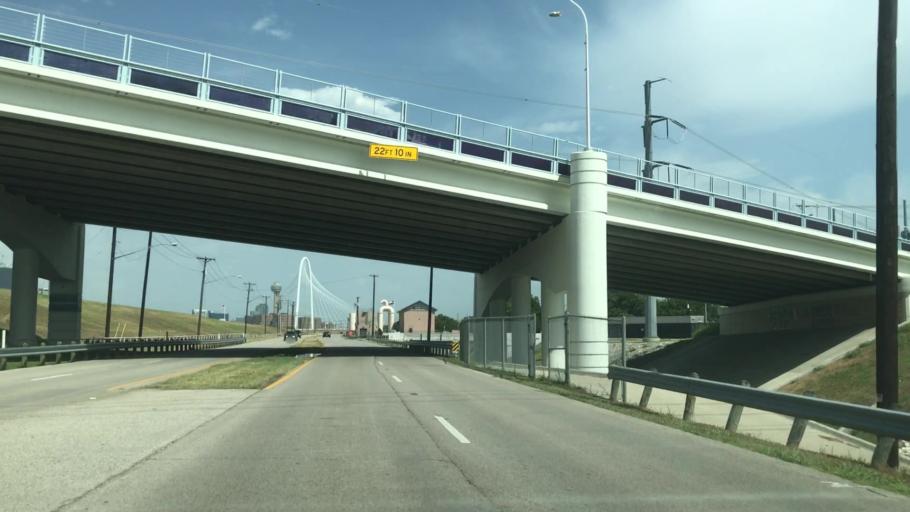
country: US
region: Texas
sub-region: Dallas County
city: Dallas
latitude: 32.7861
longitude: -96.8363
